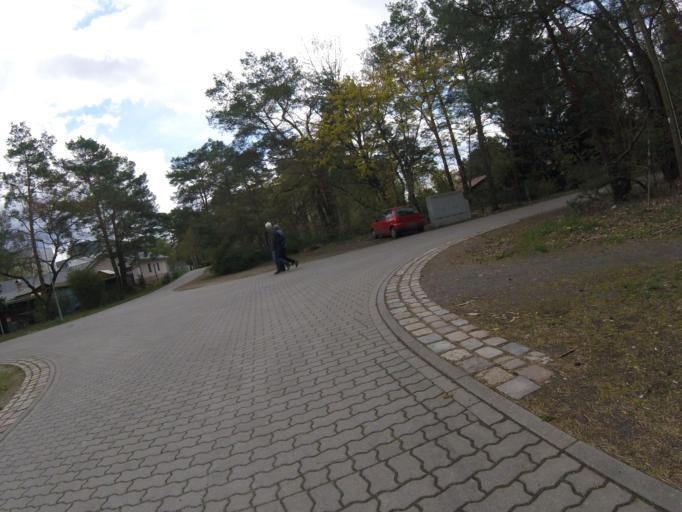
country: DE
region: Brandenburg
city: Bestensee
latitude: 52.2456
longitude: 13.6548
